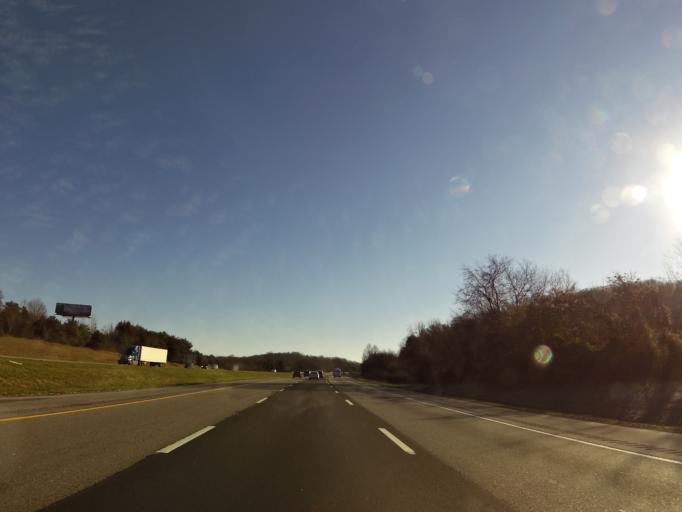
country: US
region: Tennessee
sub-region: Knox County
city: Mascot
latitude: 36.0050
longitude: -83.7492
